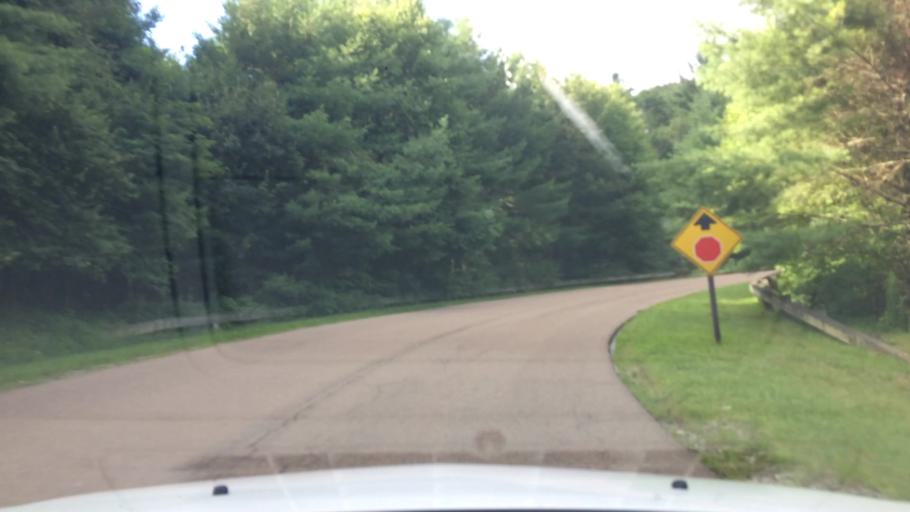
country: US
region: North Carolina
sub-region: Watauga County
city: Blowing Rock
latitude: 36.1476
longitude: -81.6644
